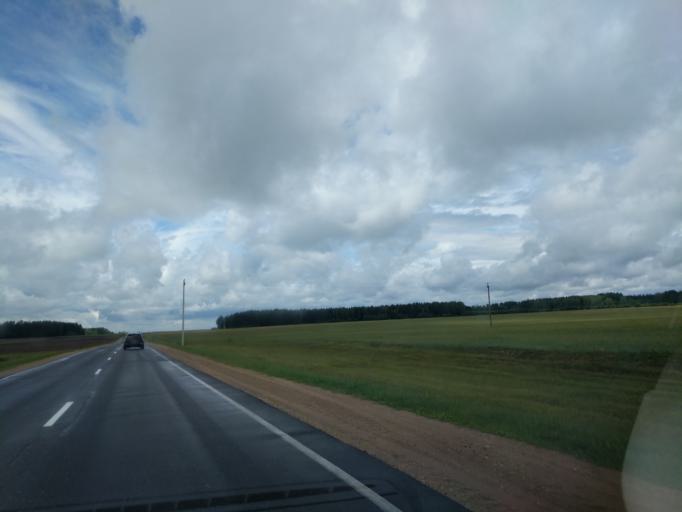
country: BY
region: Minsk
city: Il'ya
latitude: 54.3770
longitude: 27.3805
